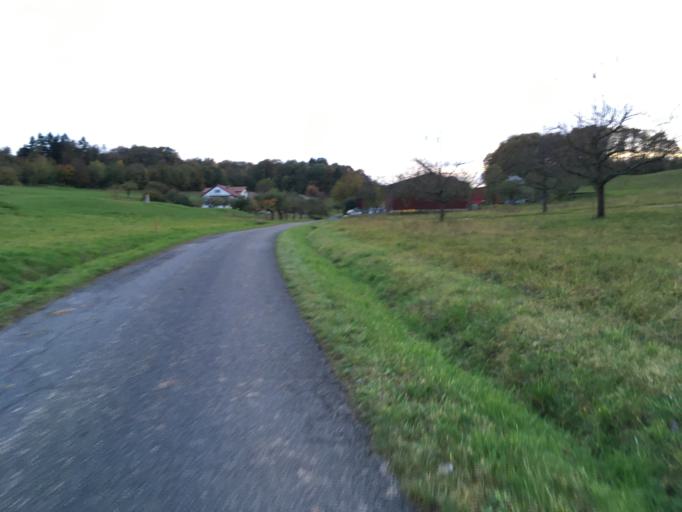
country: DE
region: Baden-Wuerttemberg
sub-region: Karlsruhe Region
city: Rosenberg
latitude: 49.3932
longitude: 9.4772
